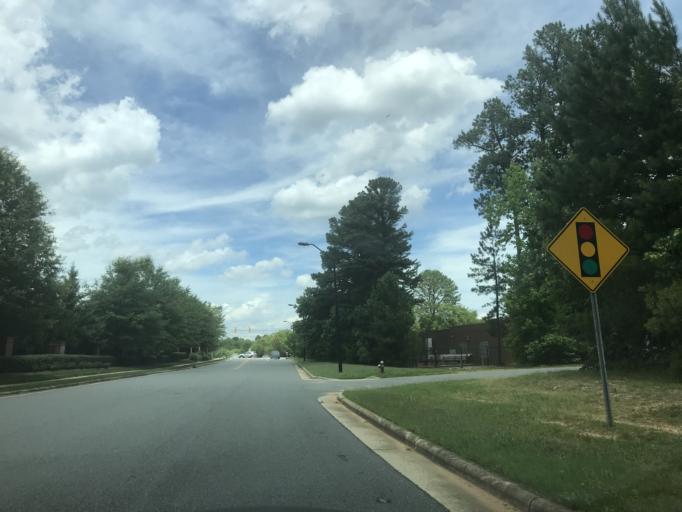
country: US
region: North Carolina
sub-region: Wake County
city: West Raleigh
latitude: 35.9007
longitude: -78.6585
